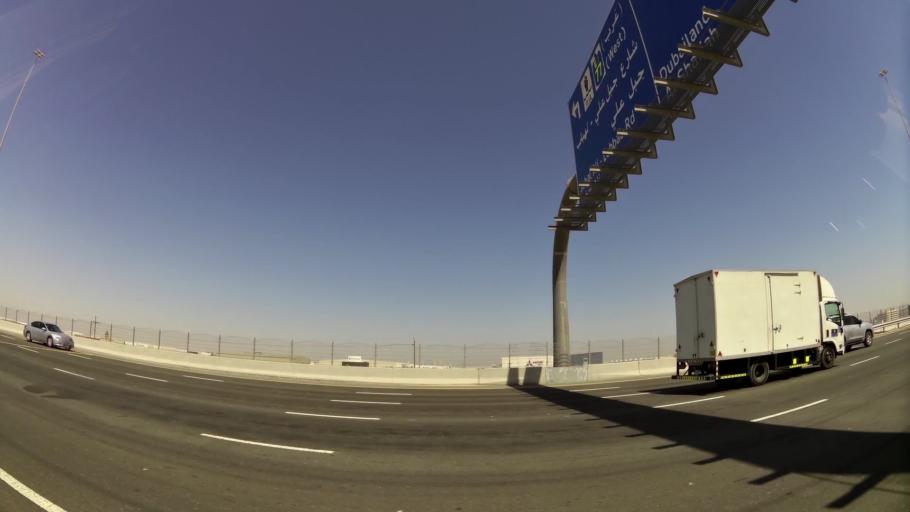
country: AE
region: Dubai
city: Dubai
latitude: 24.9698
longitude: 55.1409
